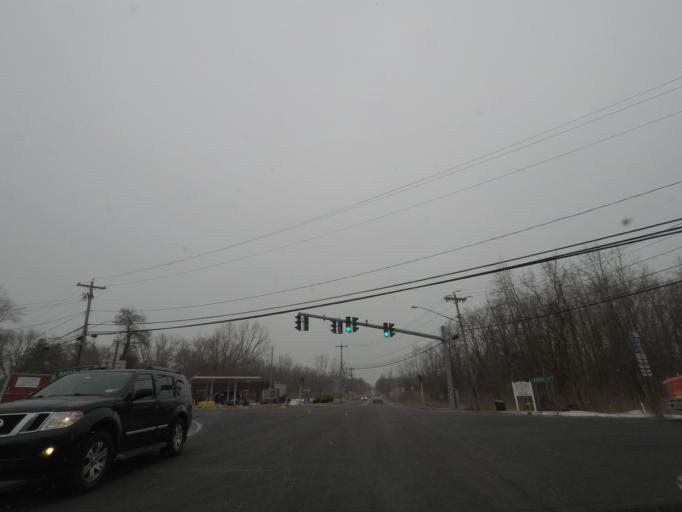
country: US
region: New York
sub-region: Rensselaer County
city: Castleton-on-Hudson
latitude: 42.5485
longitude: -73.8075
